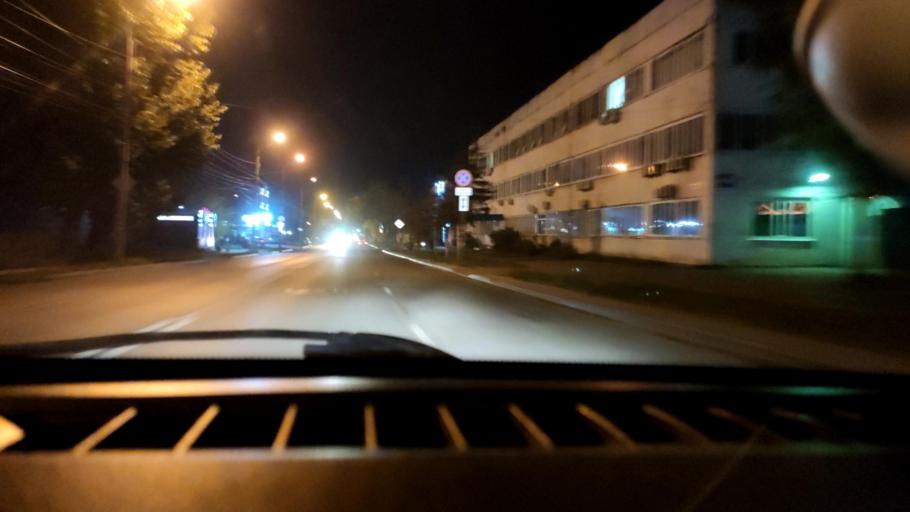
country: RU
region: Samara
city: Samara
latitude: 53.1968
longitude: 50.1846
